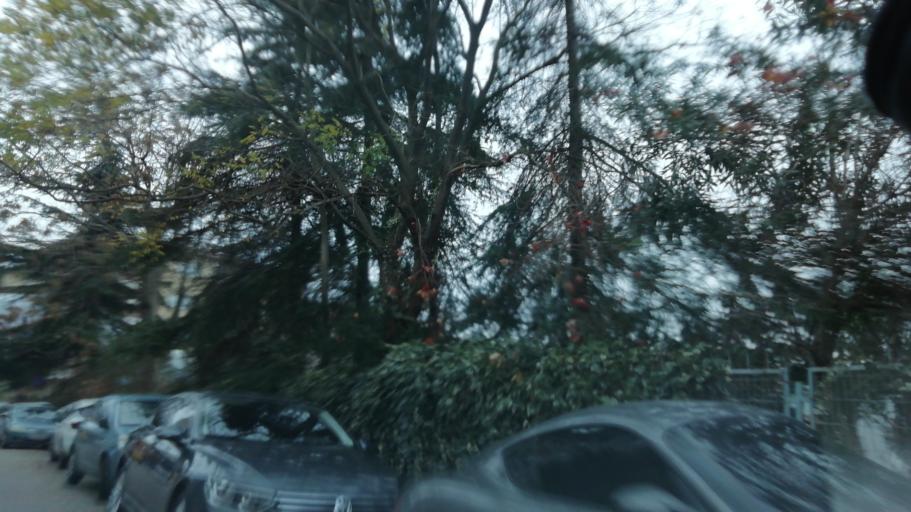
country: TR
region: Istanbul
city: Mahmutbey
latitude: 41.0175
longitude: 28.8242
